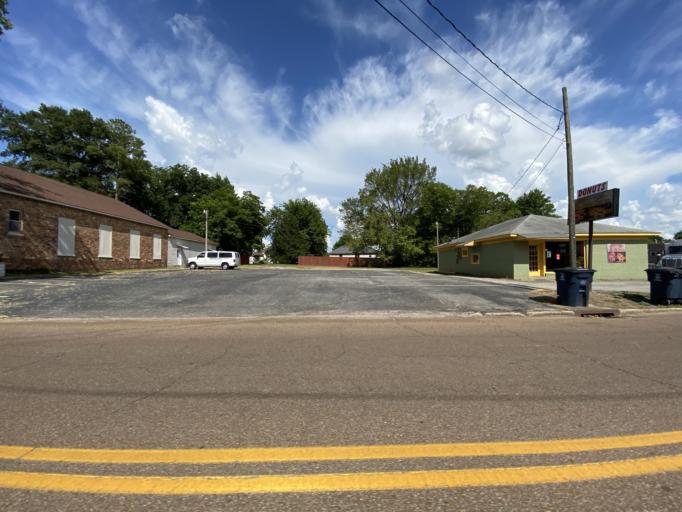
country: US
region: Tennessee
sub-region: Lauderdale County
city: Halls
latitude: 35.8736
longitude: -89.3962
